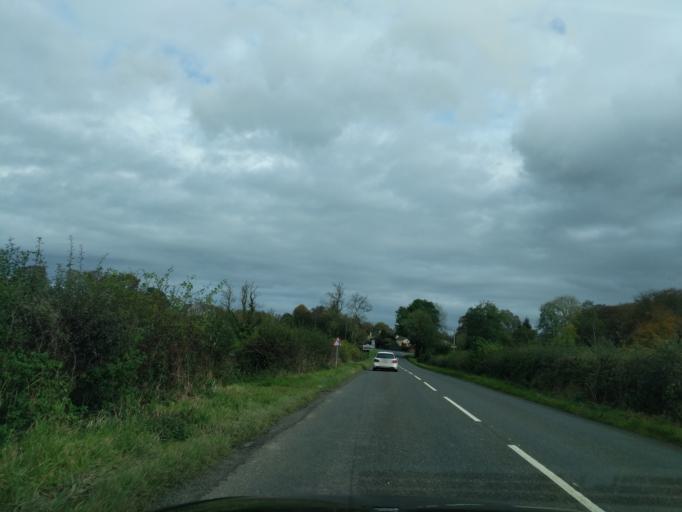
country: GB
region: Scotland
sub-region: Dumfries and Galloway
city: Castle Douglas
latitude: 54.9297
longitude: -3.9409
